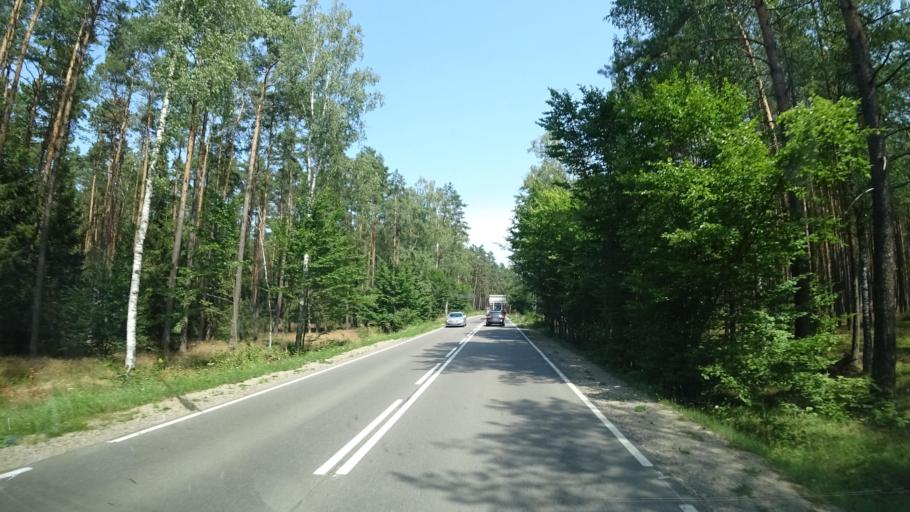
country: PL
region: Pomeranian Voivodeship
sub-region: Powiat koscierski
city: Lipusz
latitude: 54.1128
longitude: 17.8316
